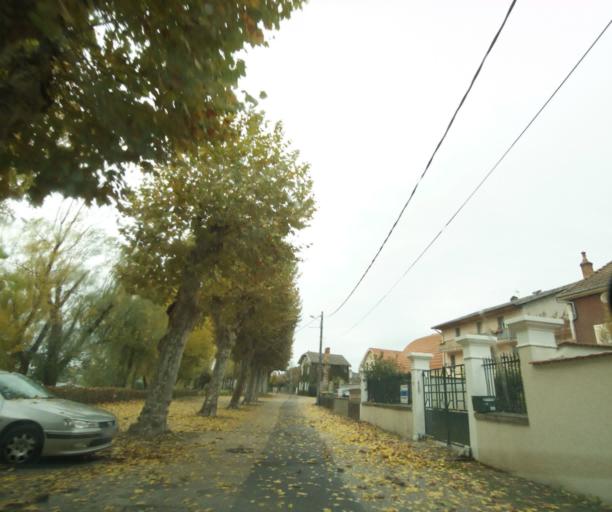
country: FR
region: Rhone-Alpes
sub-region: Departement de l'Ain
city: Loyettes
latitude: 45.7722
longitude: 5.2107
